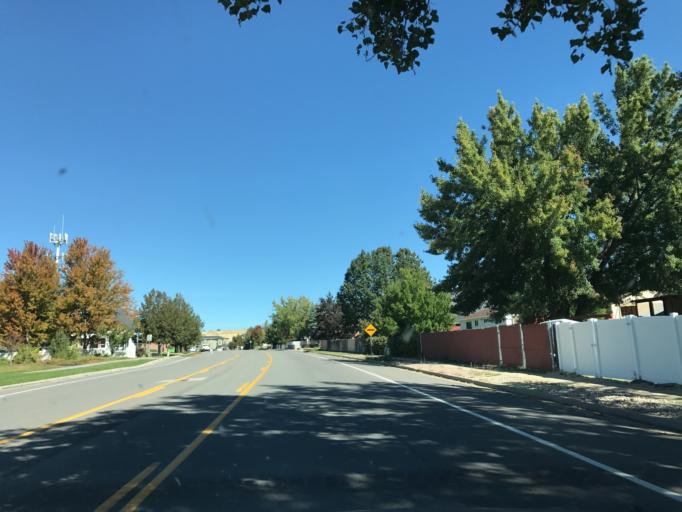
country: US
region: Utah
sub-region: Davis County
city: South Weber
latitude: 41.0981
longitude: -111.9394
